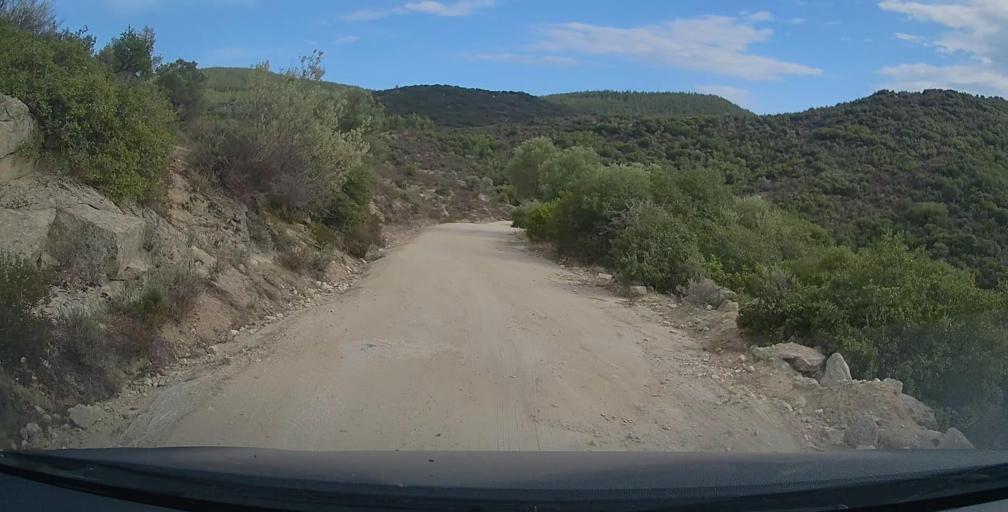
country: GR
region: Central Macedonia
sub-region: Nomos Chalkidikis
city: Sykia
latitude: 39.9907
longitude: 23.9162
